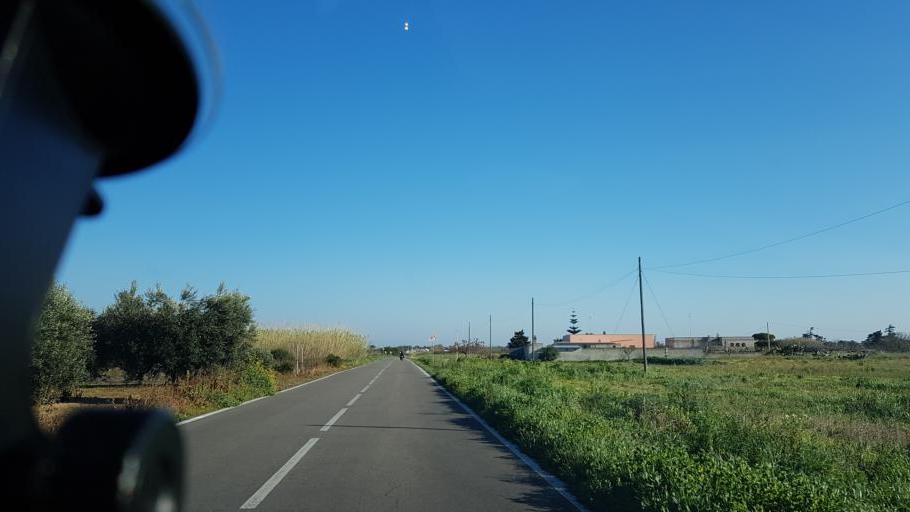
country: IT
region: Apulia
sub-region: Provincia di Lecce
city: Giorgilorio
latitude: 40.4386
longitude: 18.2369
